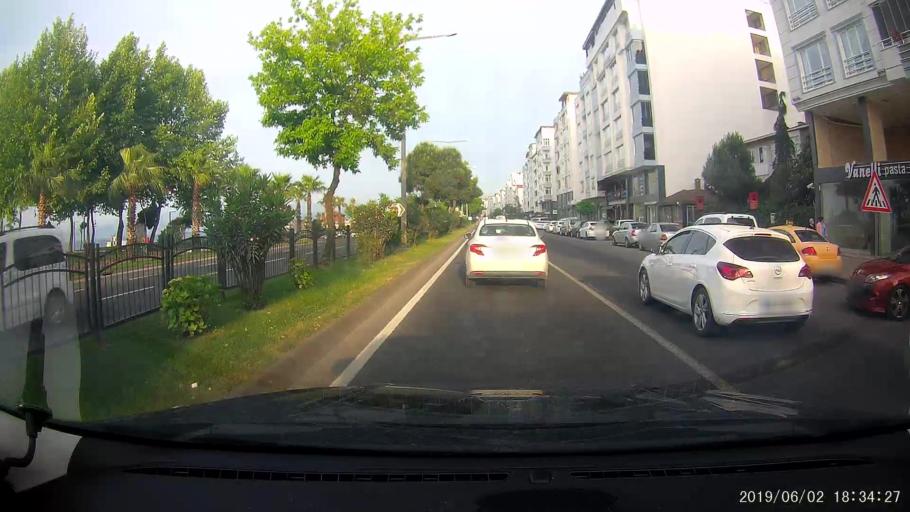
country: TR
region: Ordu
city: Fatsa
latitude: 41.0293
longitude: 37.5044
